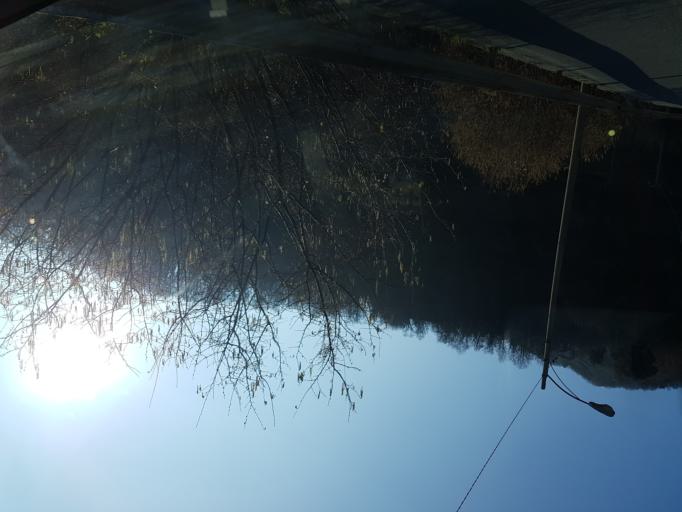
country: IT
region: Liguria
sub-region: Provincia di Genova
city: Manesseno
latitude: 44.4590
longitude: 8.9210
